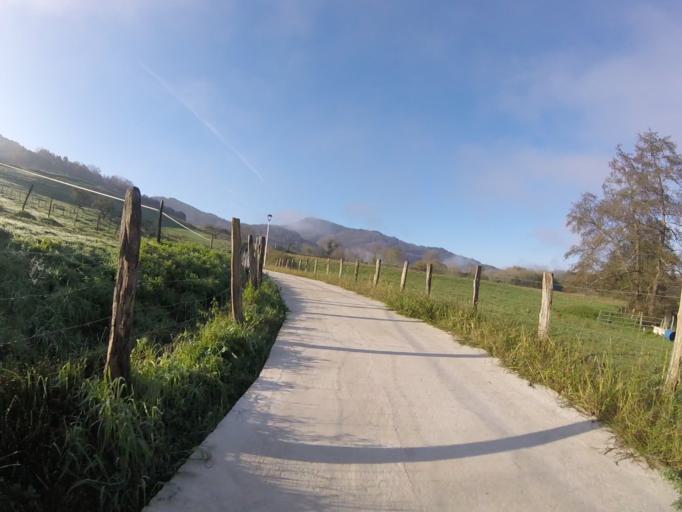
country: ES
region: Basque Country
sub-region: Provincia de Guipuzcoa
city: Usurbil
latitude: 43.2660
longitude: -2.0392
